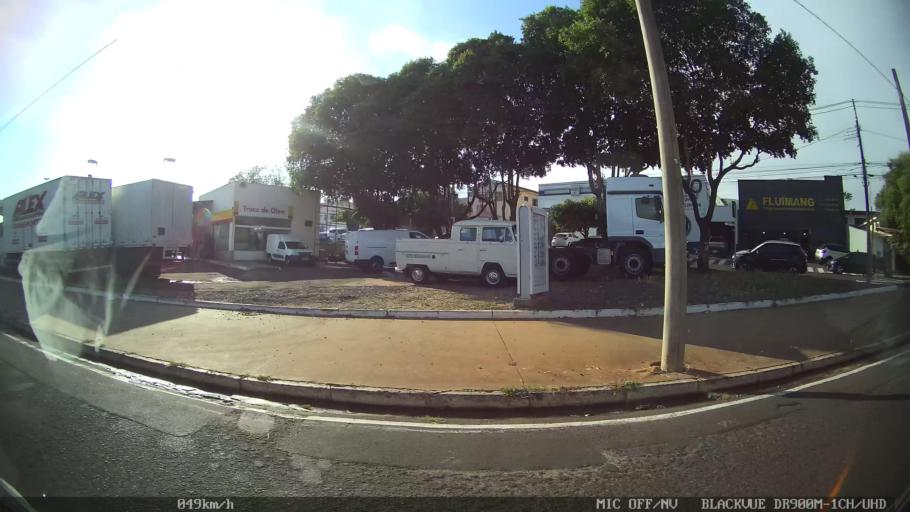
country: BR
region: Sao Paulo
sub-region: Sao Jose Do Rio Preto
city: Sao Jose do Rio Preto
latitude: -20.8282
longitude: -49.3661
